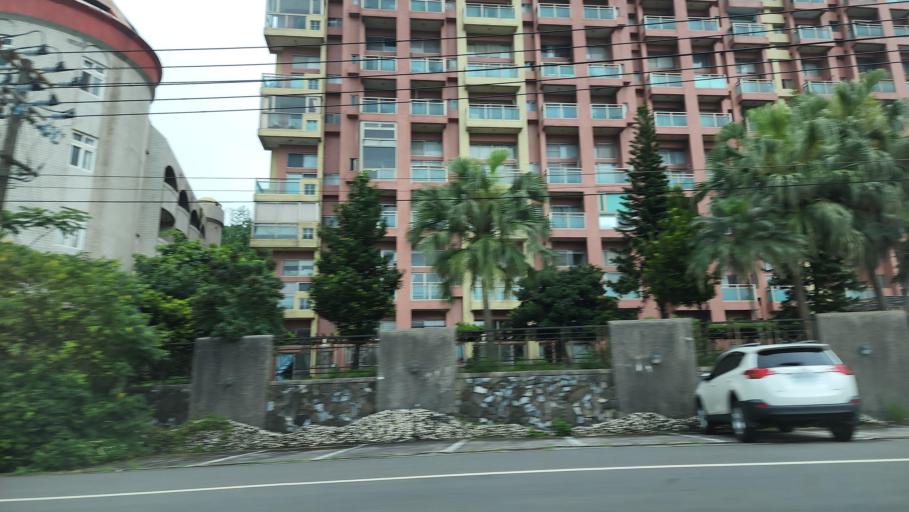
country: TW
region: Taiwan
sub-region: Keelung
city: Keelung
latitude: 25.1928
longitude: 121.6803
